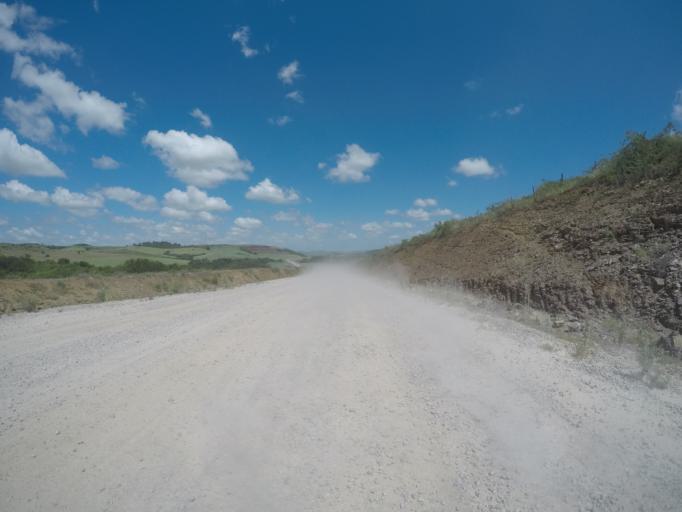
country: ZA
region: KwaZulu-Natal
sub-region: uThungulu District Municipality
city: Empangeni
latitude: -28.6383
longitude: 31.7638
